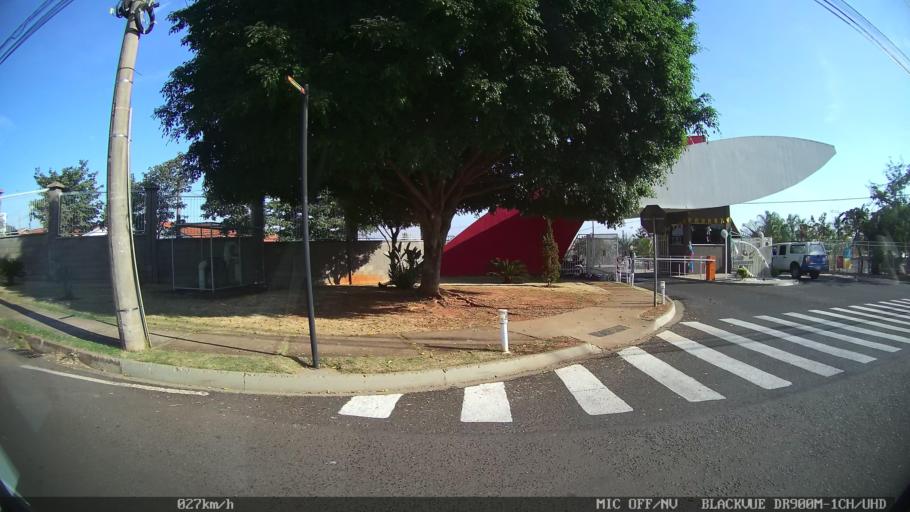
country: BR
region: Sao Paulo
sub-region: Sao Jose Do Rio Preto
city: Sao Jose do Rio Preto
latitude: -20.7710
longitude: -49.3317
